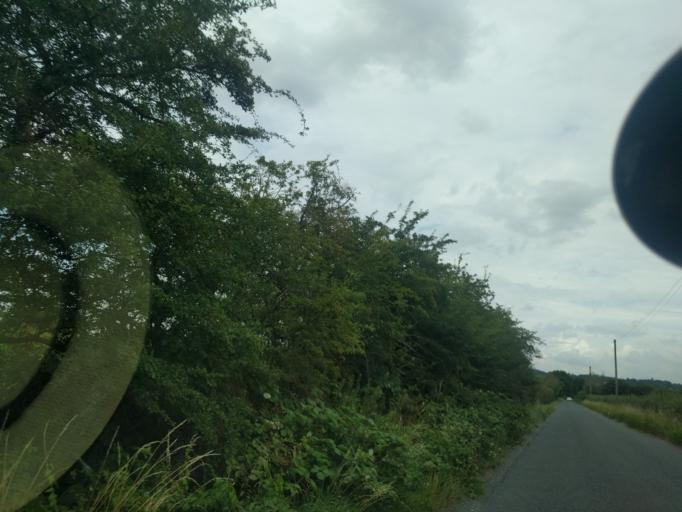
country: GB
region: England
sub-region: Wiltshire
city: Lacock
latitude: 51.3912
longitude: -2.1082
